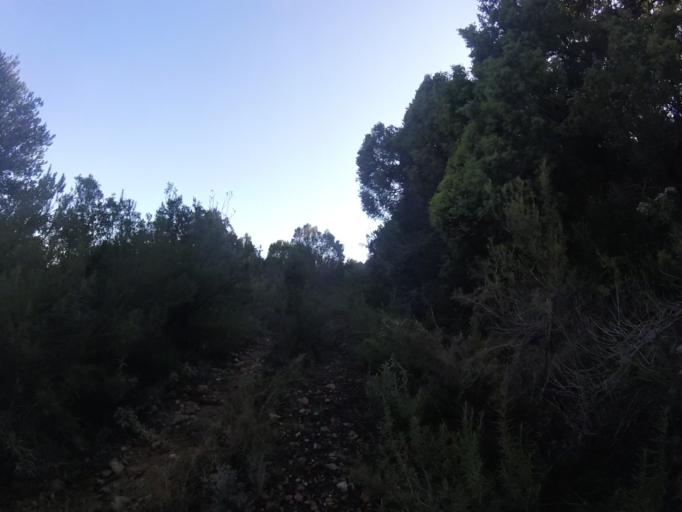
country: ES
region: Valencia
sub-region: Provincia de Castello
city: Sarratella
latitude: 40.2927
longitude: 0.0506
